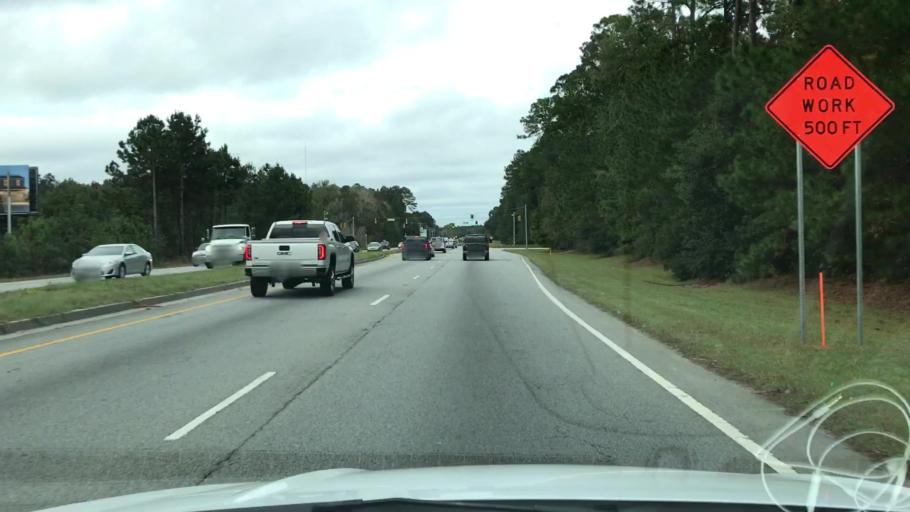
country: US
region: South Carolina
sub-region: Beaufort County
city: Bluffton
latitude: 32.3099
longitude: -80.9347
